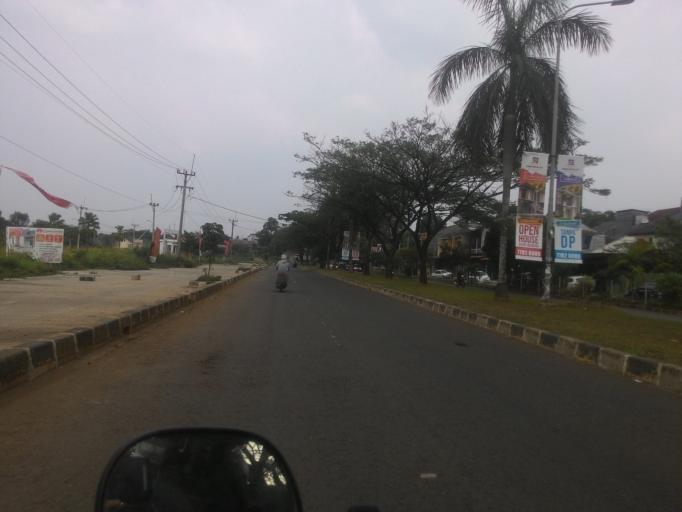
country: ID
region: West Java
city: Depok
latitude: -6.4408
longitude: 106.8272
